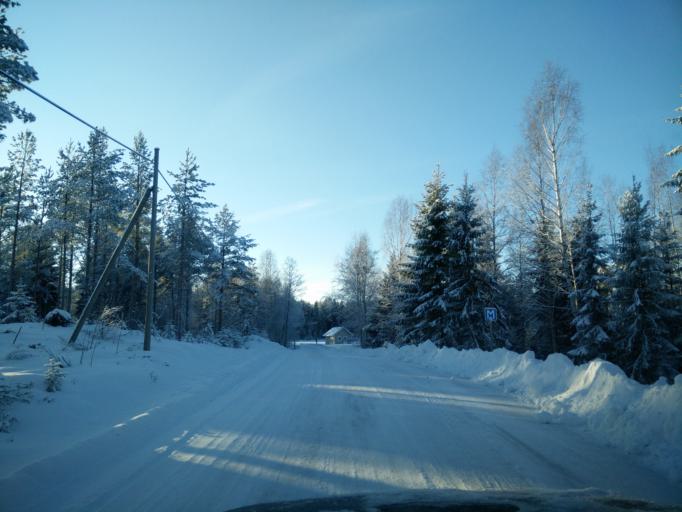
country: SE
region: Vaesternorrland
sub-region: Sundsvalls Kommun
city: Njurundabommen
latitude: 62.2327
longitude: 17.5085
